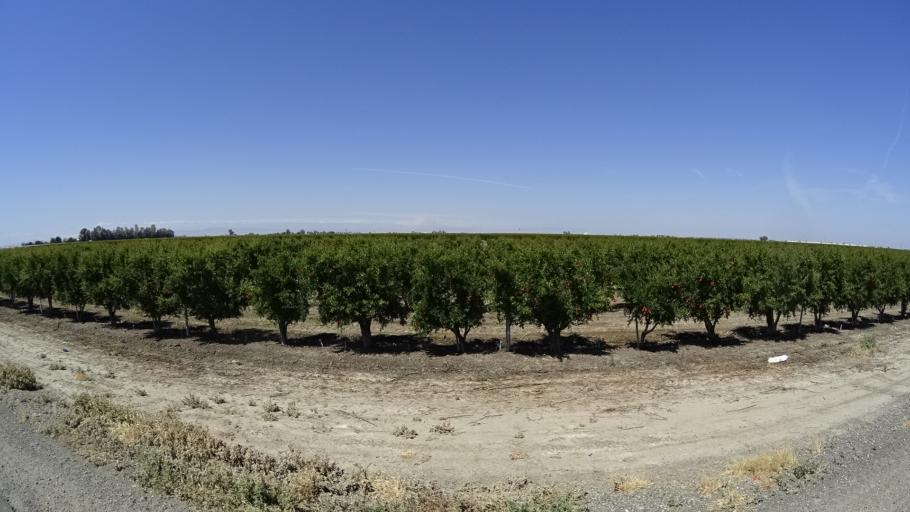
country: US
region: California
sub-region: Kings County
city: Stratford
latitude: 36.2171
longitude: -119.7981
